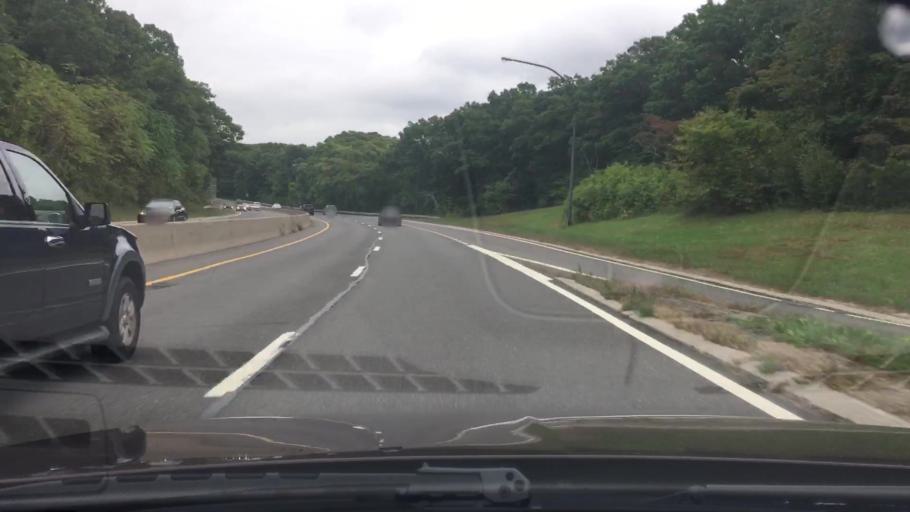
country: US
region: New York
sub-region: Nassau County
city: Plainview
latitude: 40.7991
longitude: -73.4664
